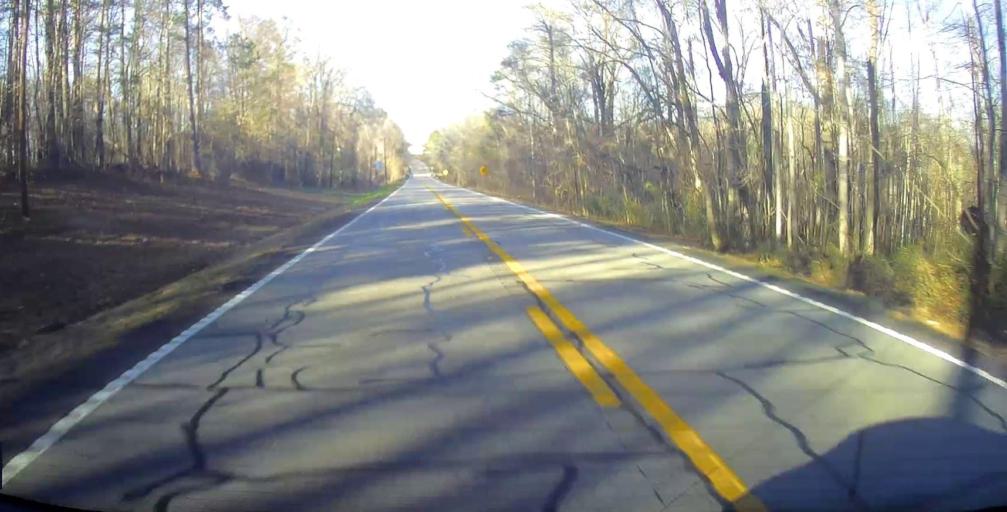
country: US
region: Georgia
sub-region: Meriwether County
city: Manchester
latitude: 32.8701
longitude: -84.5981
